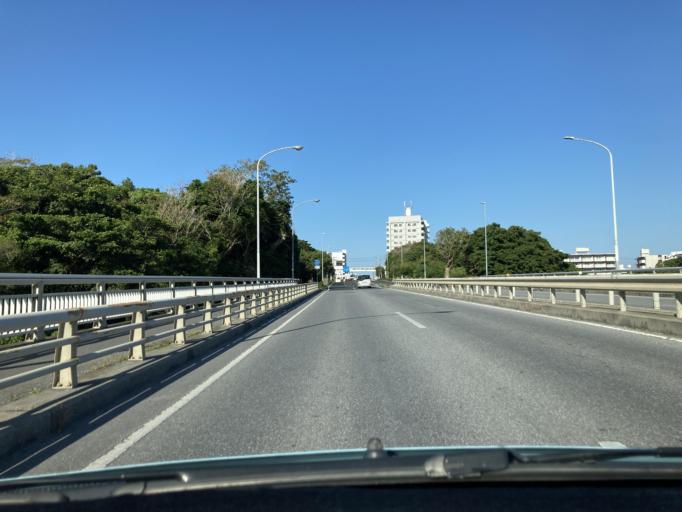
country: JP
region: Okinawa
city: Ginowan
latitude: 26.2524
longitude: 127.7512
